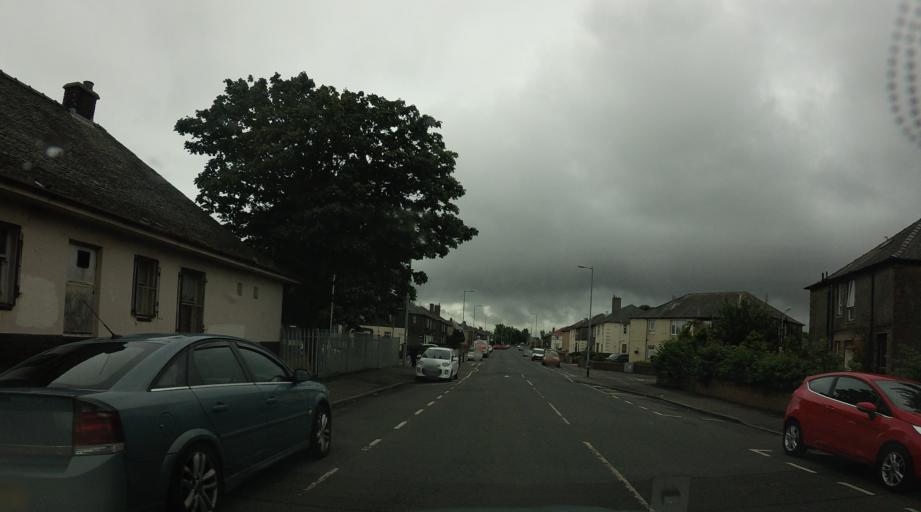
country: GB
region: Scotland
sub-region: South Ayrshire
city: Prestwick
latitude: 55.4711
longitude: -4.6155
